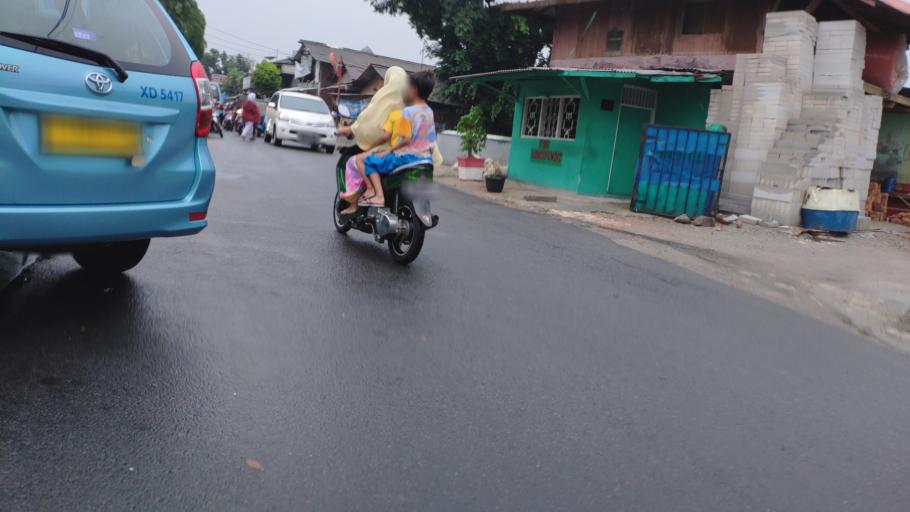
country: ID
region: Jakarta Raya
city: Jakarta
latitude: -6.2033
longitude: 106.8689
